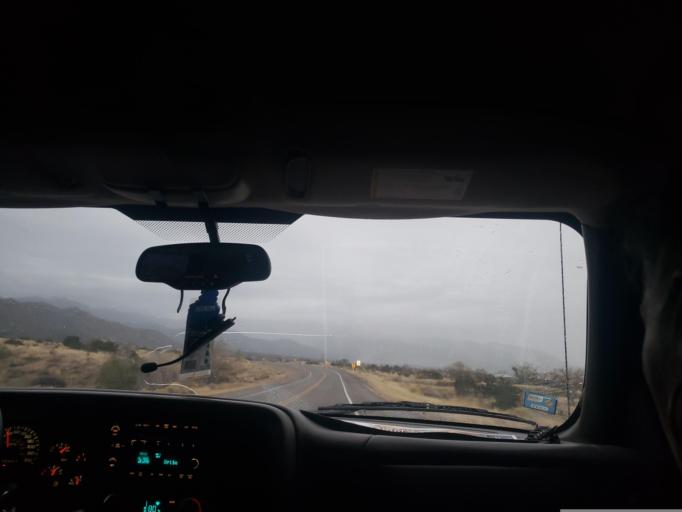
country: US
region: New Mexico
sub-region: Bernalillo County
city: Sandia Heights
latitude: 35.1980
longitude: -106.5039
